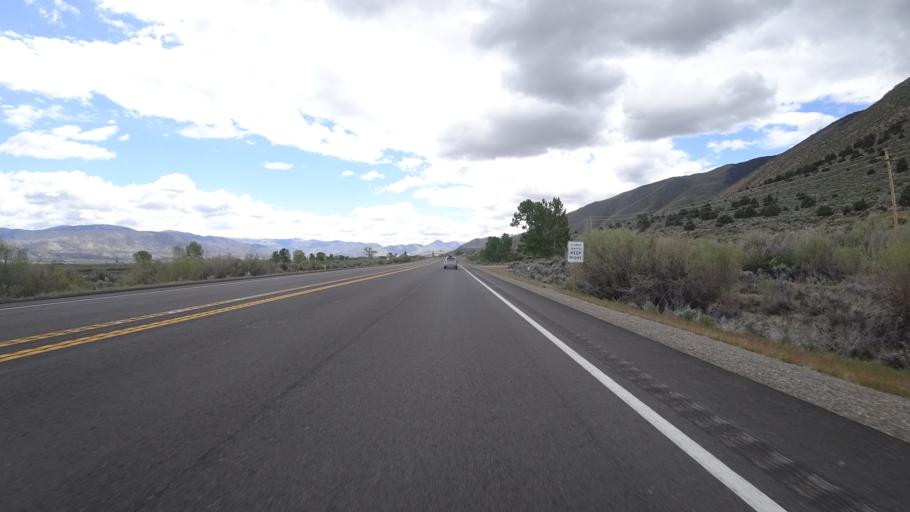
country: US
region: Nevada
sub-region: Lyon County
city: Smith Valley
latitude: 38.6054
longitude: -119.5189
